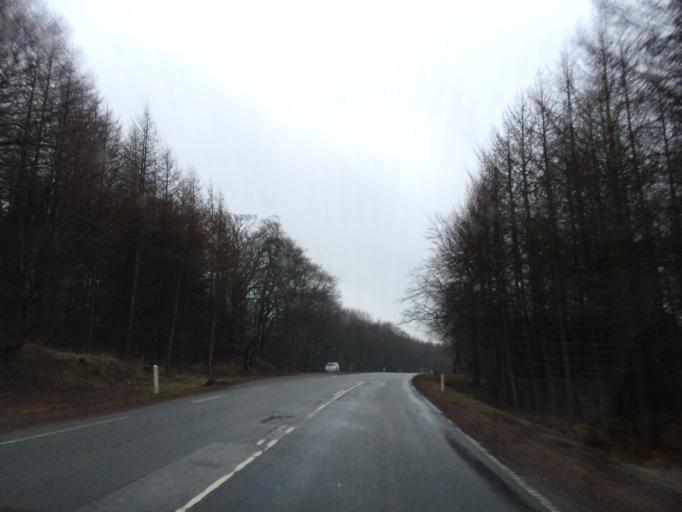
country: DK
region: North Denmark
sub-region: Mariagerfjord Kommune
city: Arden
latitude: 56.7944
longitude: 9.8209
